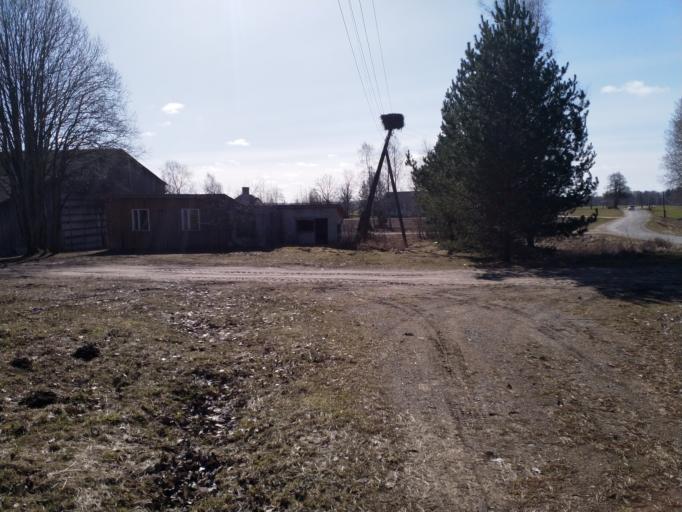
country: LV
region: Aizpute
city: Aizpute
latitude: 56.8287
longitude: 21.7752
